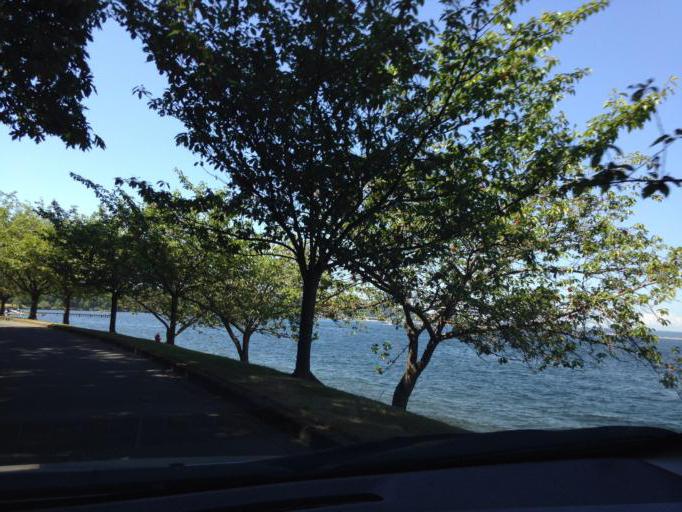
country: US
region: Washington
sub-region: King County
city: Mercer Island
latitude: 47.5694
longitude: -122.2742
